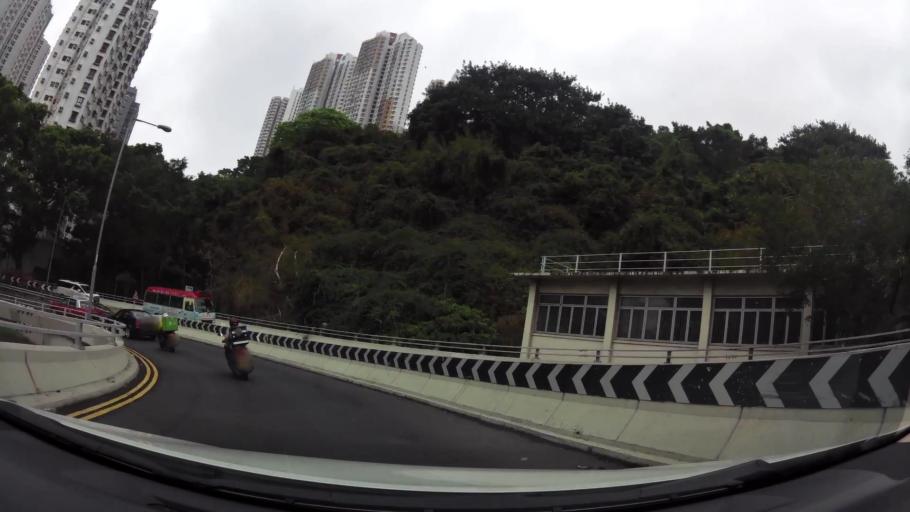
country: HK
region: Central and Western
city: Central
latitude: 22.2486
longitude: 114.1601
